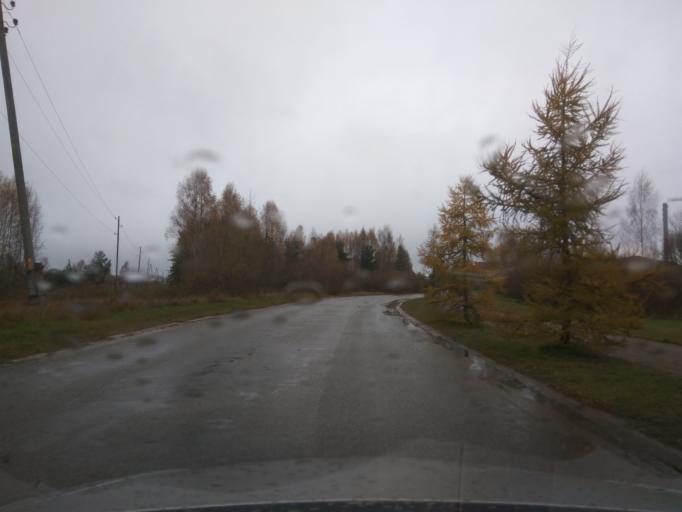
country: LV
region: Kuldigas Rajons
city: Kuldiga
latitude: 56.9710
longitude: 21.9459
